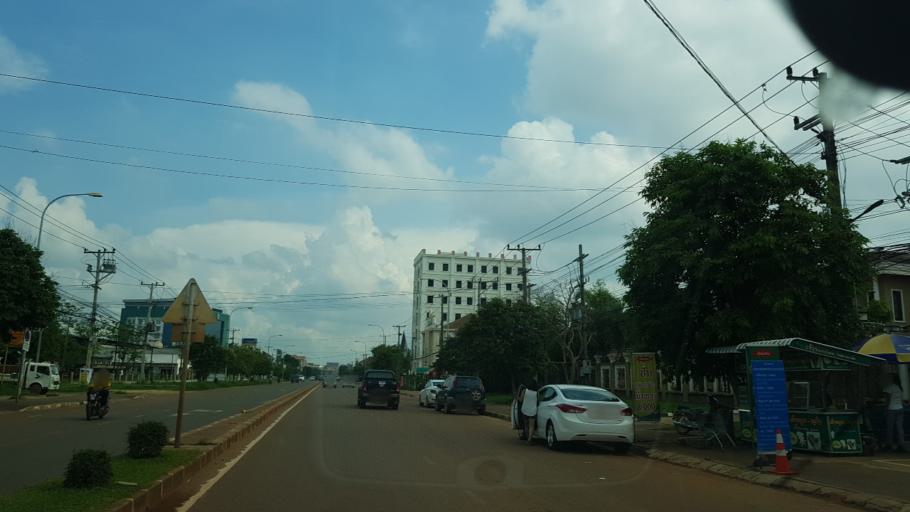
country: LA
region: Vientiane
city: Vientiane
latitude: 18.0286
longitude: 102.6517
